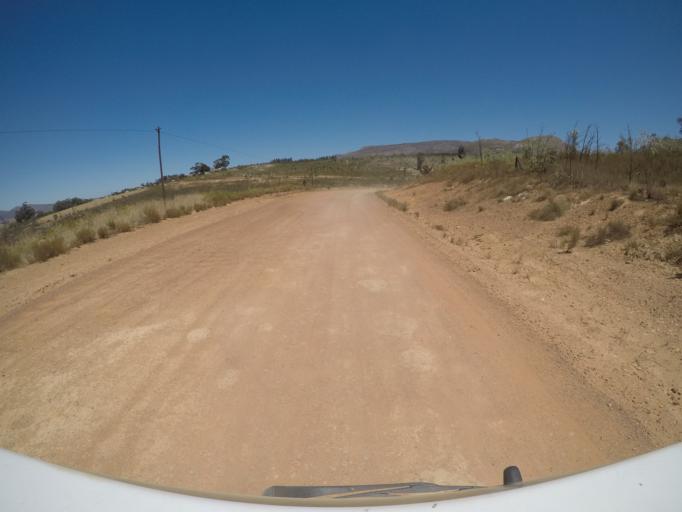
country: ZA
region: Western Cape
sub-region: Overberg District Municipality
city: Hermanus
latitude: -34.2178
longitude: 19.2073
